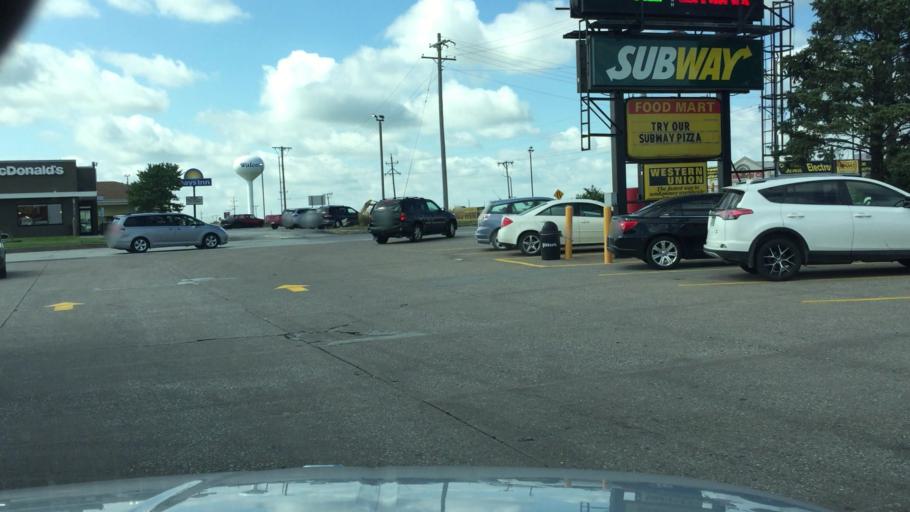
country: US
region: Iowa
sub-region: Scott County
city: Walcott
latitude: 41.6144
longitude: -90.7826
